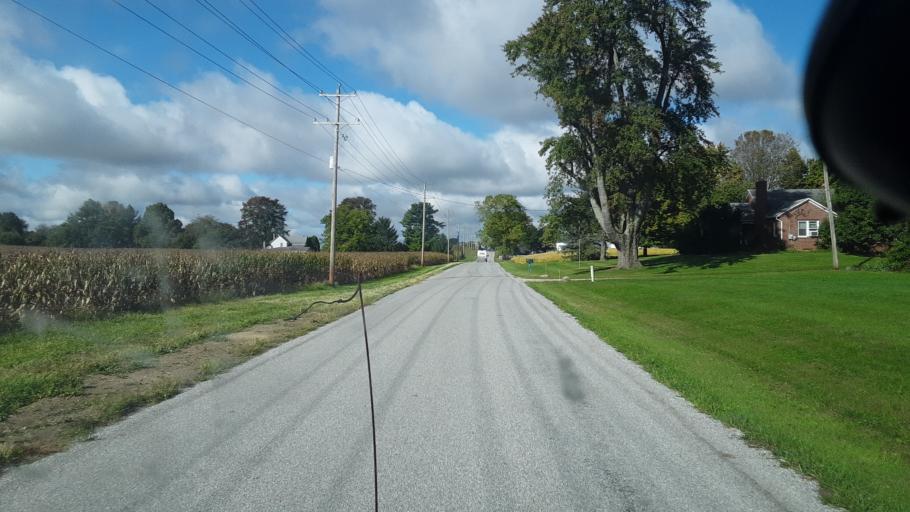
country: US
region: Ohio
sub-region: Knox County
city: Centerburg
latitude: 40.2590
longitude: -82.7051
